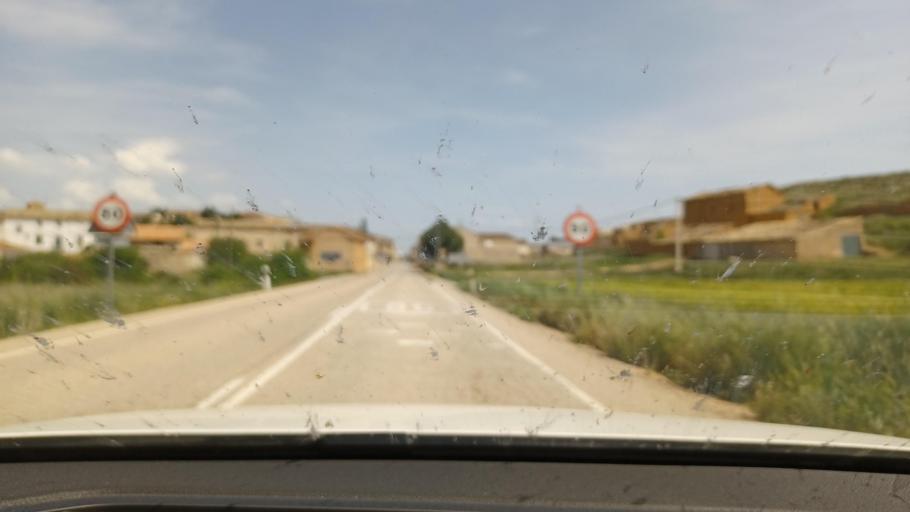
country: ES
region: Castille and Leon
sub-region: Provincia de Soria
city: Monteagudo de las Vicarias
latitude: 41.3670
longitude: -2.1725
